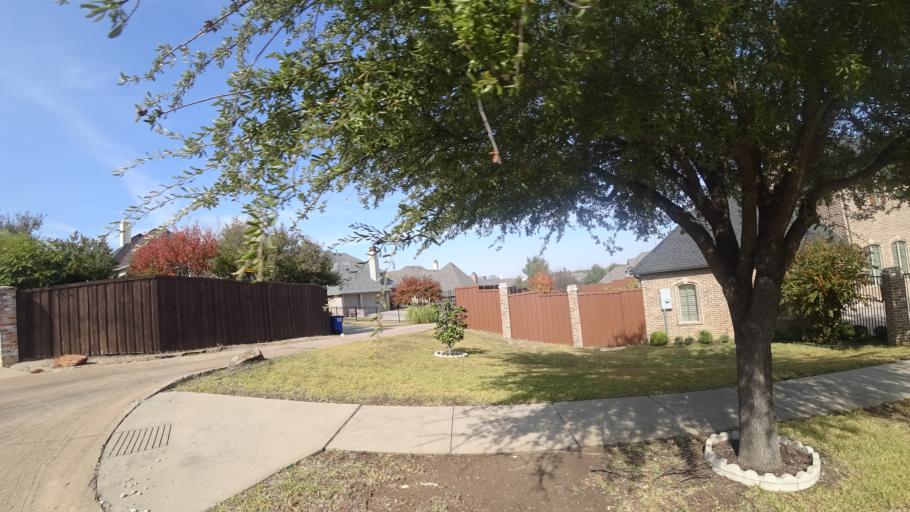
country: US
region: Texas
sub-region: Denton County
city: The Colony
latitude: 33.0381
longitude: -96.8925
